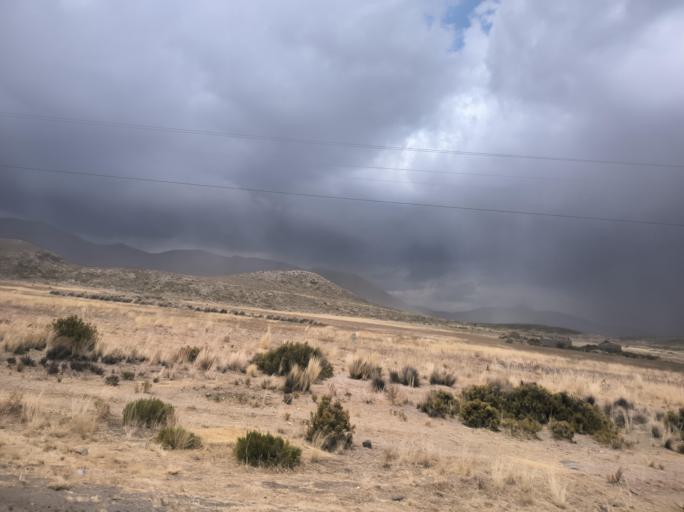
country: BO
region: Oruro
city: Challapata
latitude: -18.7584
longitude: -66.8614
